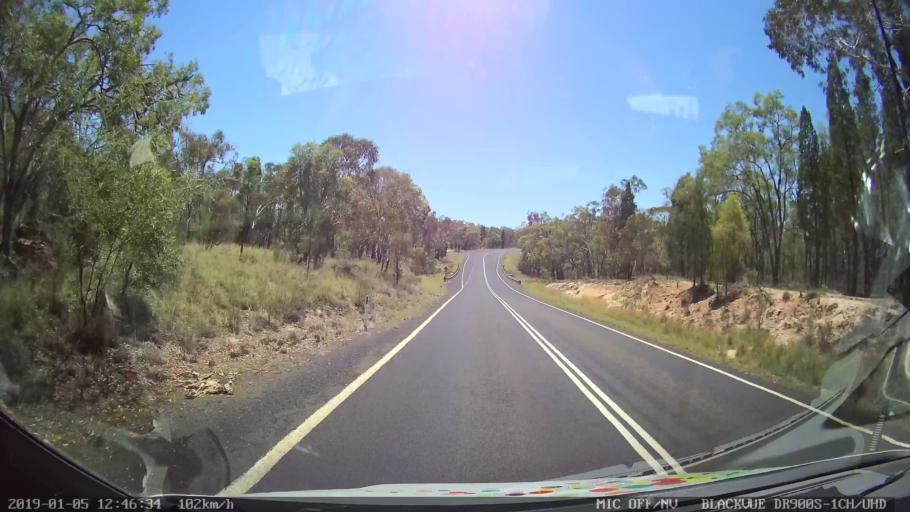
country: AU
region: New South Wales
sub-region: Warrumbungle Shire
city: Coonabarabran
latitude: -31.1166
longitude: 149.5643
